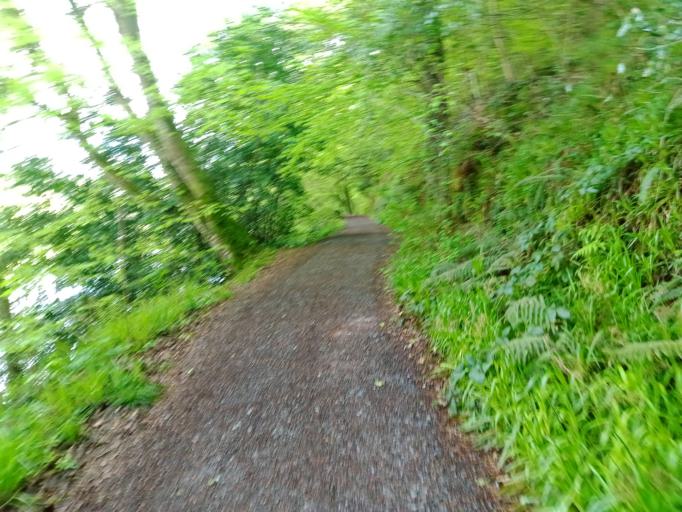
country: IE
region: Leinster
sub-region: Kilkenny
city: Thomastown
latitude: 52.4823
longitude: -7.0614
